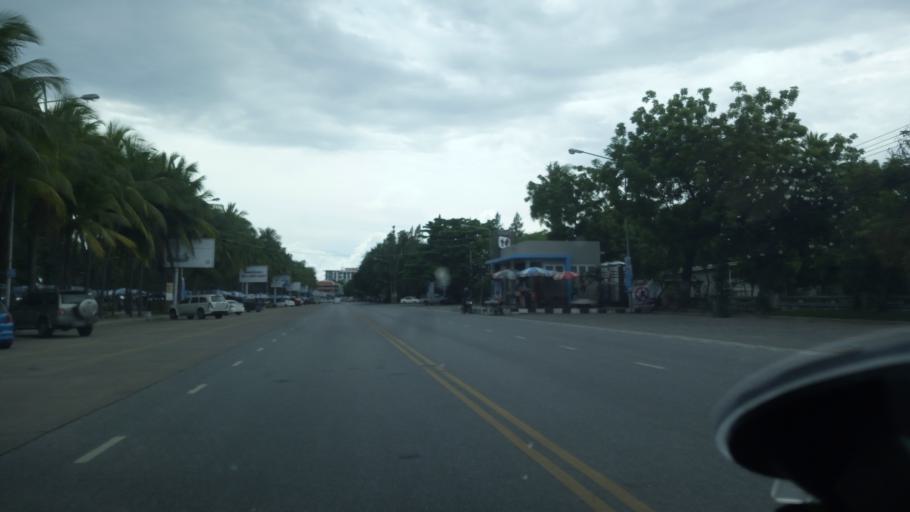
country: TH
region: Chon Buri
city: Chon Buri
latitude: 13.2958
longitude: 100.9052
